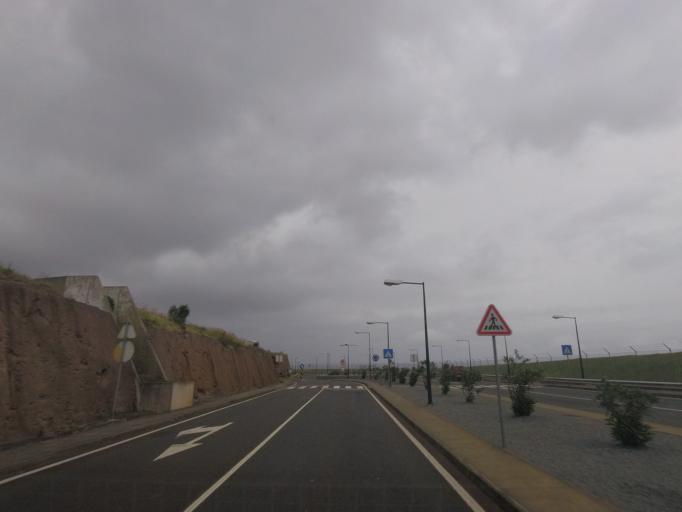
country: PT
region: Madeira
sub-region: Machico
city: Machico
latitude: 32.7083
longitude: -16.7633
